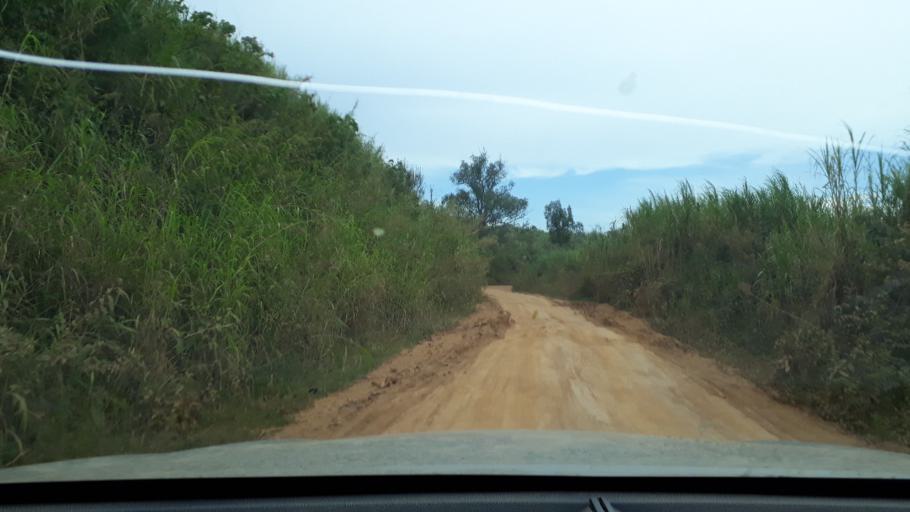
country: CD
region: Eastern Province
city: Bunia
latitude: 1.8247
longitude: 30.4434
